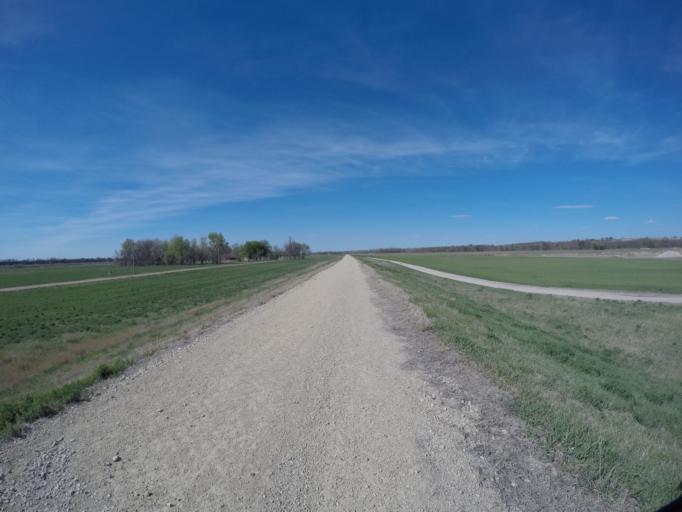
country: US
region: Kansas
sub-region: Saline County
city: Salina
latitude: 38.7836
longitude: -97.5761
